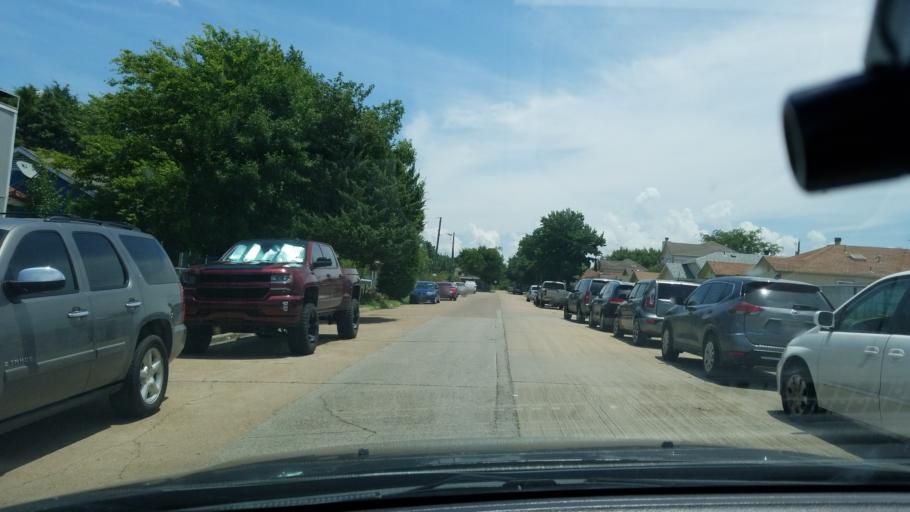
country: US
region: Texas
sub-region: Dallas County
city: Balch Springs
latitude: 32.7447
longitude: -96.6459
